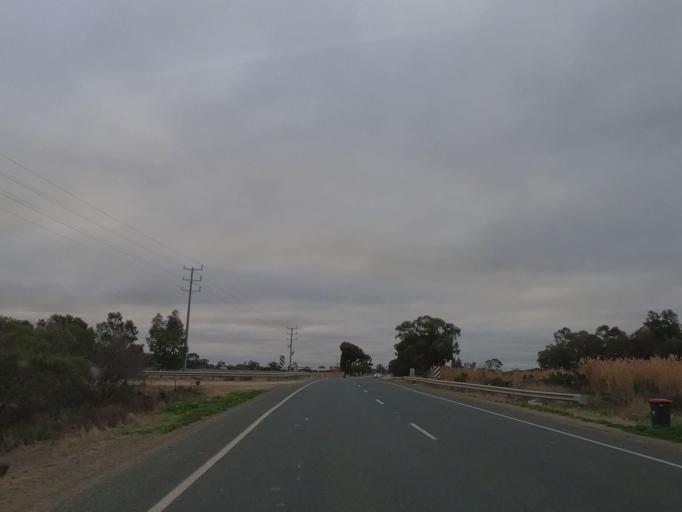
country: AU
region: Victoria
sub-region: Swan Hill
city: Swan Hill
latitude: -35.3954
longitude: 143.5729
